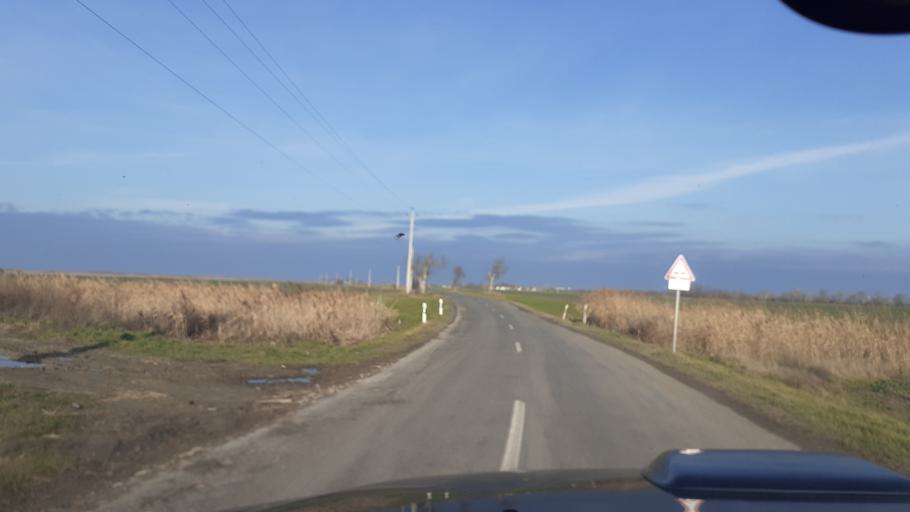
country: HU
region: Pest
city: Domsod
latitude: 47.0932
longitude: 19.0445
